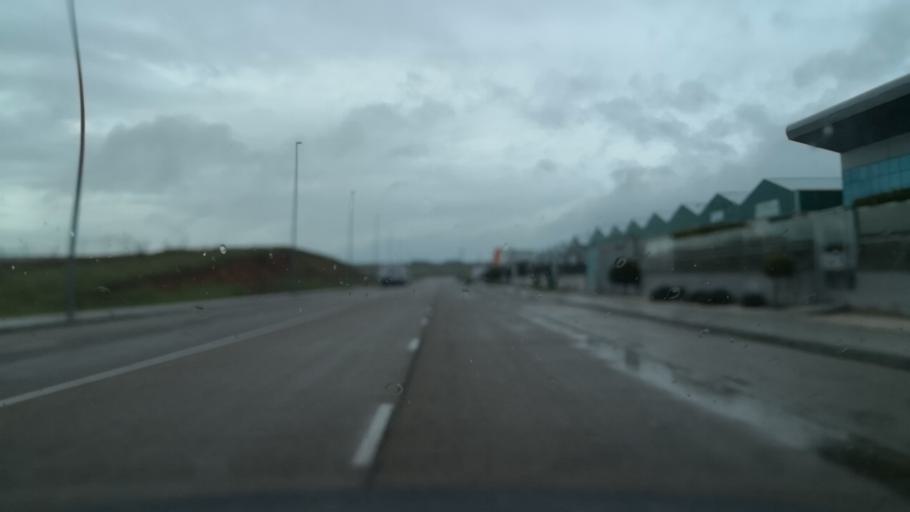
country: ES
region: Extremadura
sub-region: Provincia de Badajoz
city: Badajoz
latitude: 38.8986
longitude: -6.9938
